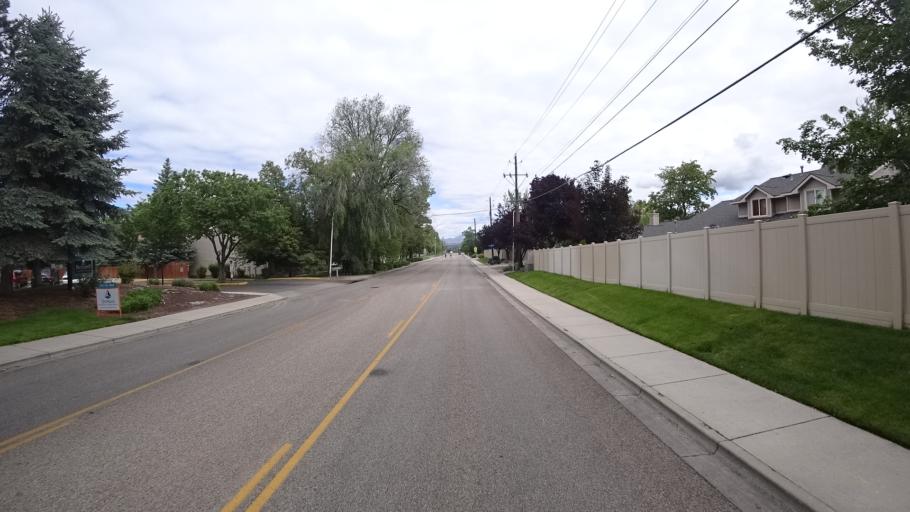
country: US
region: Idaho
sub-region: Ada County
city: Boise
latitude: 43.5741
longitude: -116.1734
